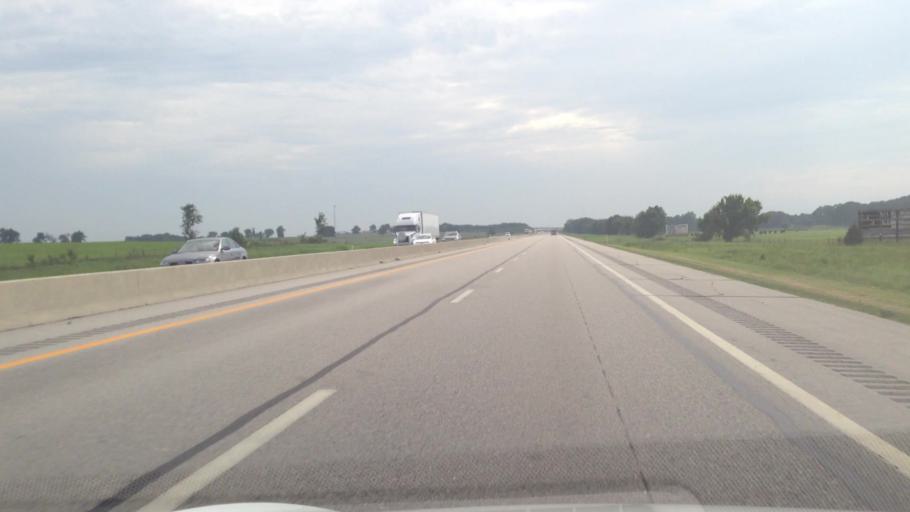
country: US
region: Kansas
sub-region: Cherokee County
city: Baxter Springs
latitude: 36.9572
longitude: -94.6673
